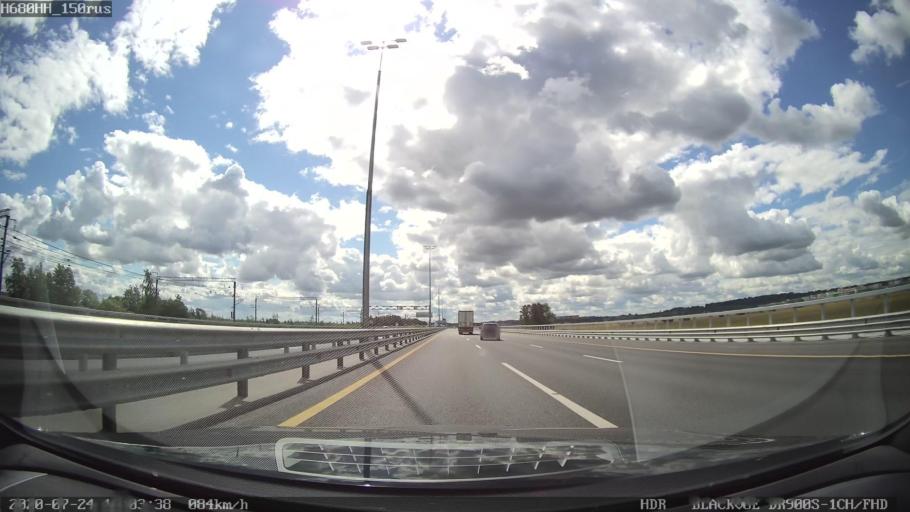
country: RU
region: St.-Petersburg
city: Shushary
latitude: 59.8004
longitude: 30.3398
